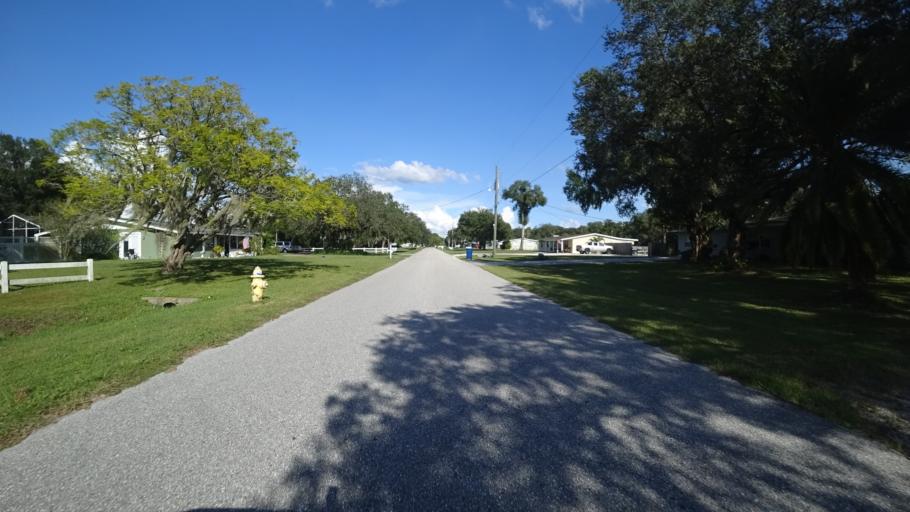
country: US
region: Florida
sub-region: Manatee County
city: Samoset
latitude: 27.4572
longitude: -82.4831
